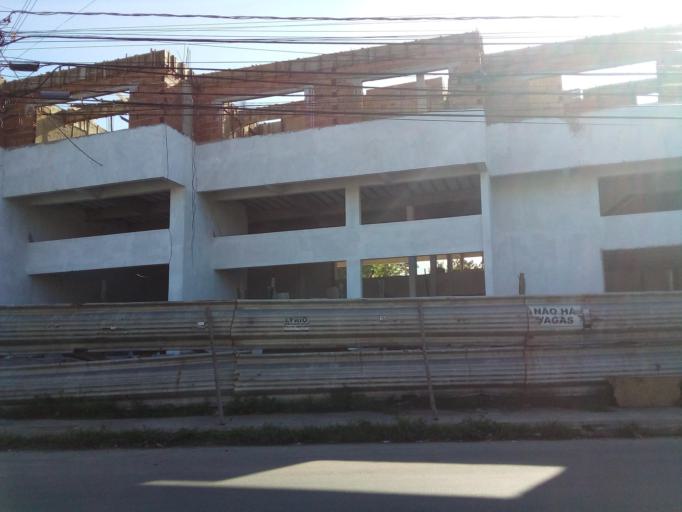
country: BR
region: Espirito Santo
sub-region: Vitoria
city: Vitoria
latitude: -20.3114
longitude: -40.3696
